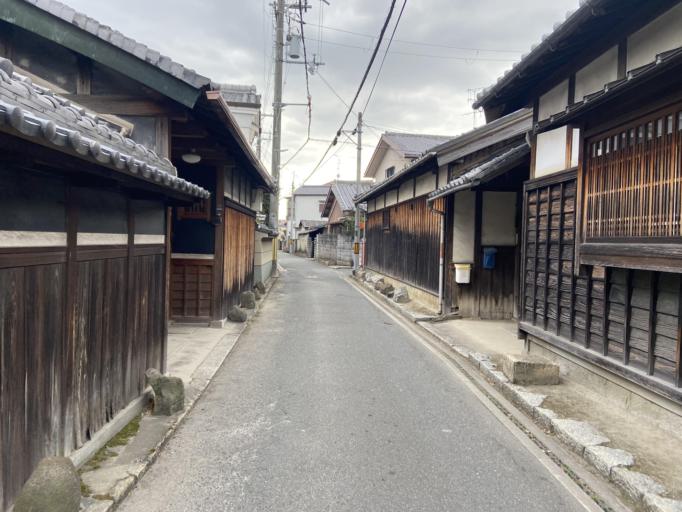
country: JP
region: Osaka
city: Hirakata
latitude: 34.7941
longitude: 135.6729
